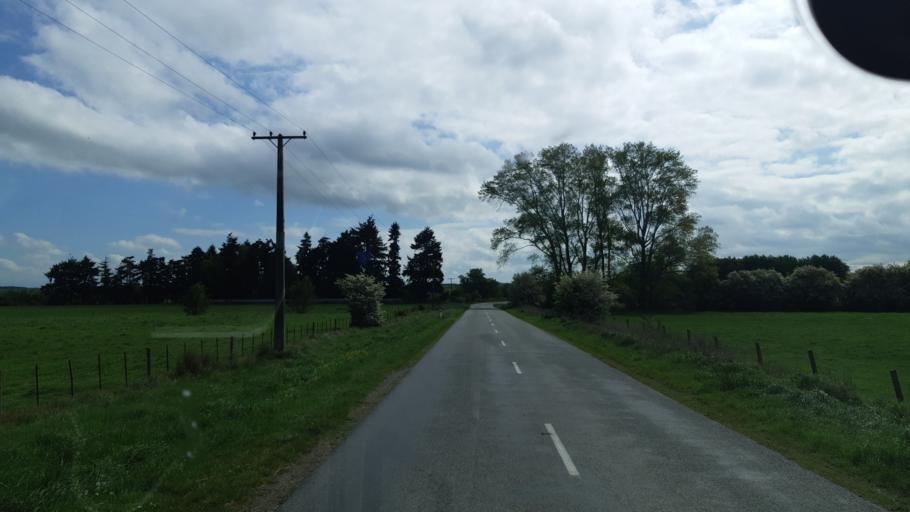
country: NZ
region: Canterbury
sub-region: Timaru District
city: Pleasant Point
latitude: -44.1723
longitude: 171.2187
